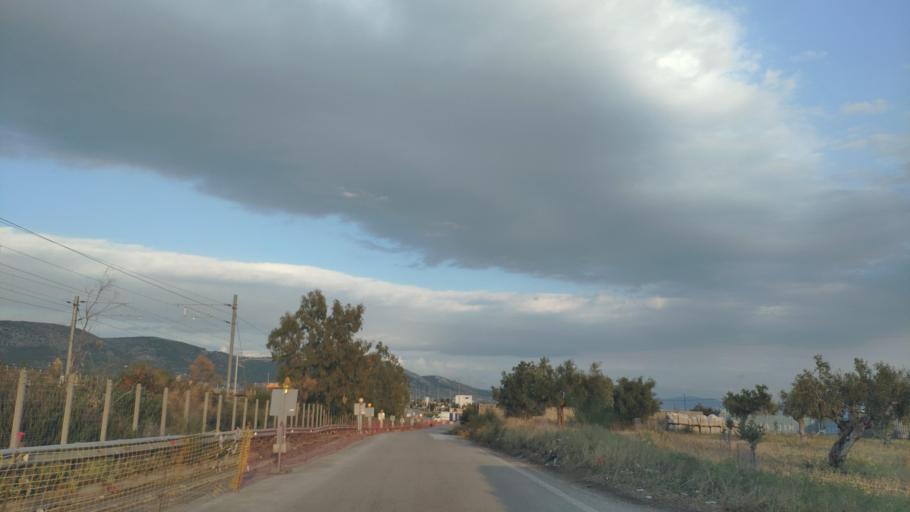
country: GR
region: Attica
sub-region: Nomarchia Dytikis Attikis
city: Nea Peramos
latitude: 38.0097
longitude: 23.4067
